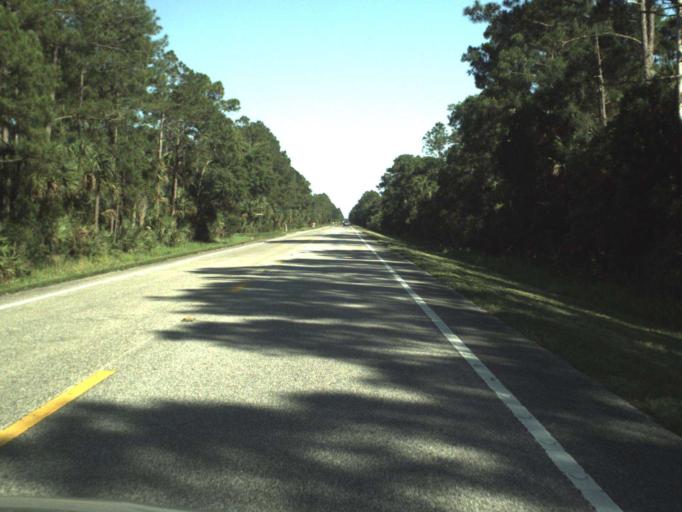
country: US
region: Florida
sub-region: Seminole County
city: Geneva
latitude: 28.6908
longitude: -80.9969
